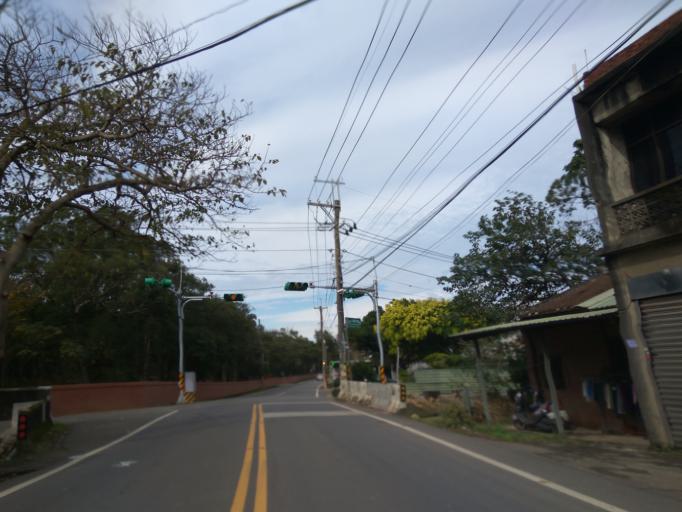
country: TW
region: Taiwan
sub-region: Hsinchu
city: Zhubei
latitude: 24.9552
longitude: 121.1237
